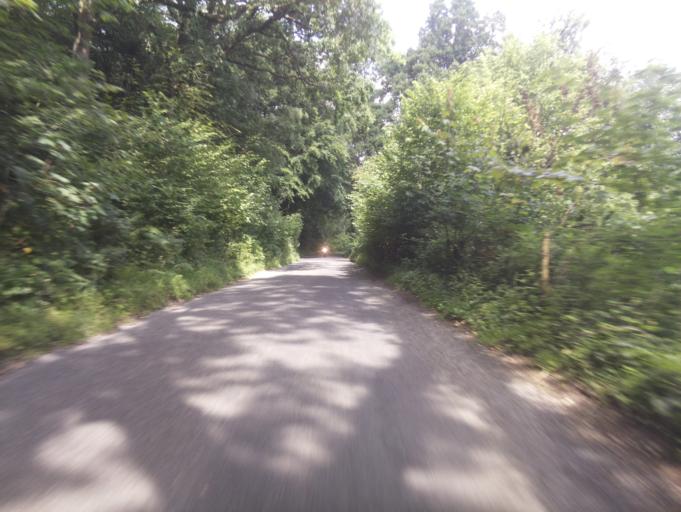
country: GB
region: England
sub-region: Gloucestershire
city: Bream
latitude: 51.7399
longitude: -2.5558
